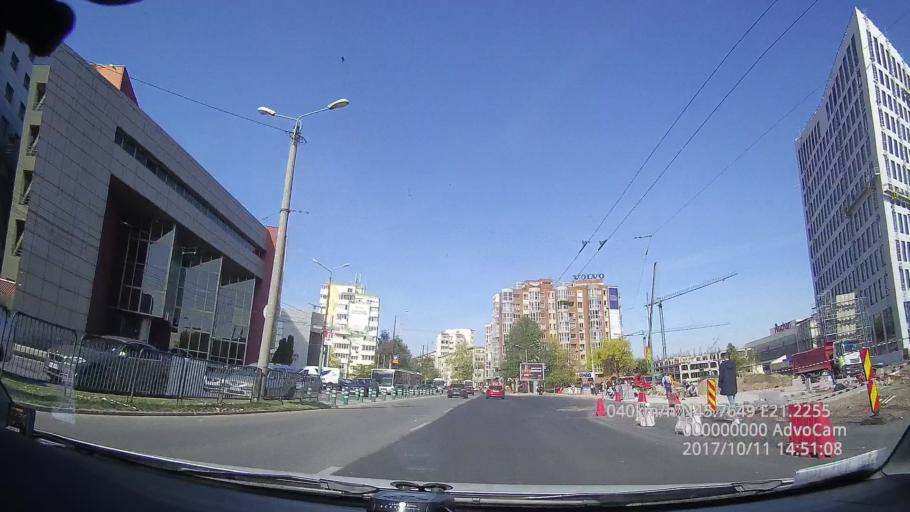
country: RO
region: Timis
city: Timisoara
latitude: 45.7651
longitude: 21.2255
